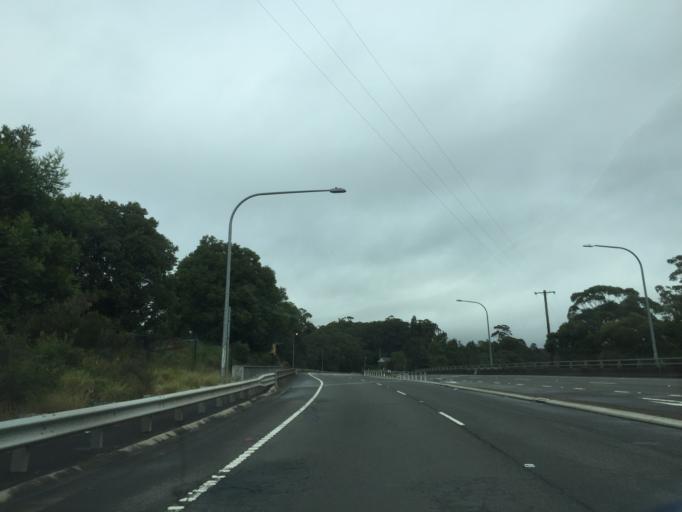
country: AU
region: New South Wales
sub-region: Blue Mountains Municipality
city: Hazelbrook
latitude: -33.7135
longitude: 150.5145
